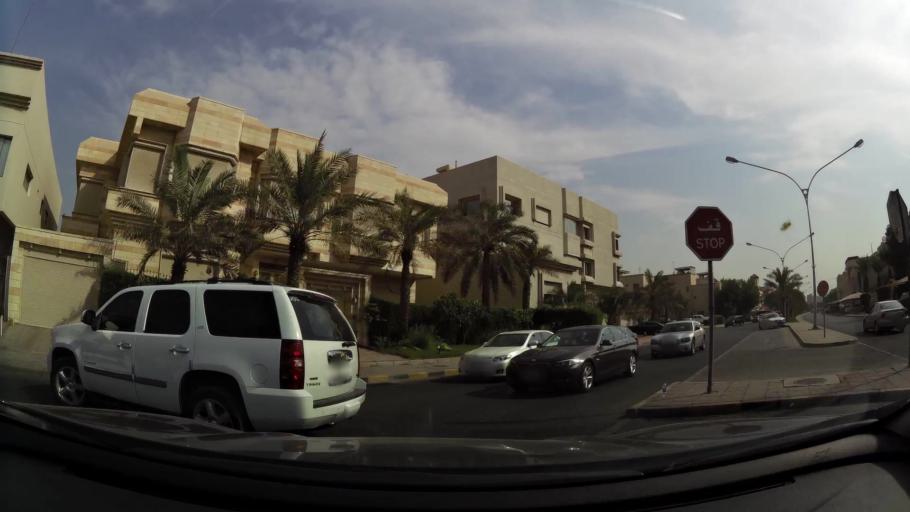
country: KW
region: Al Farwaniyah
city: Al Farwaniyah
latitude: 29.3080
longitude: 47.9710
